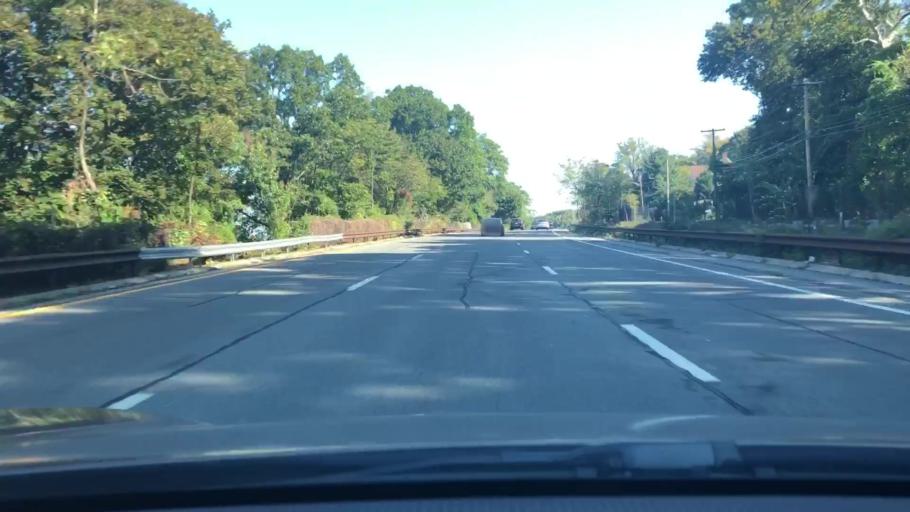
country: US
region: New York
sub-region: Westchester County
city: Tuckahoe
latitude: 40.9725
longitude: -73.8476
